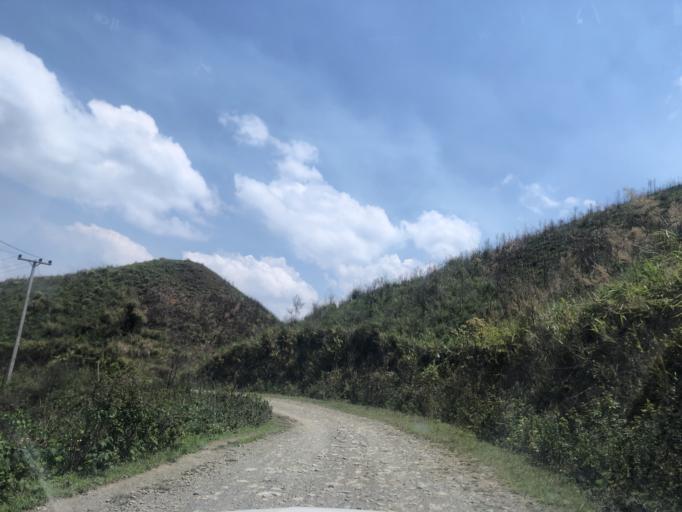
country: LA
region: Phongsali
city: Phongsali
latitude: 21.4128
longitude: 102.1866
